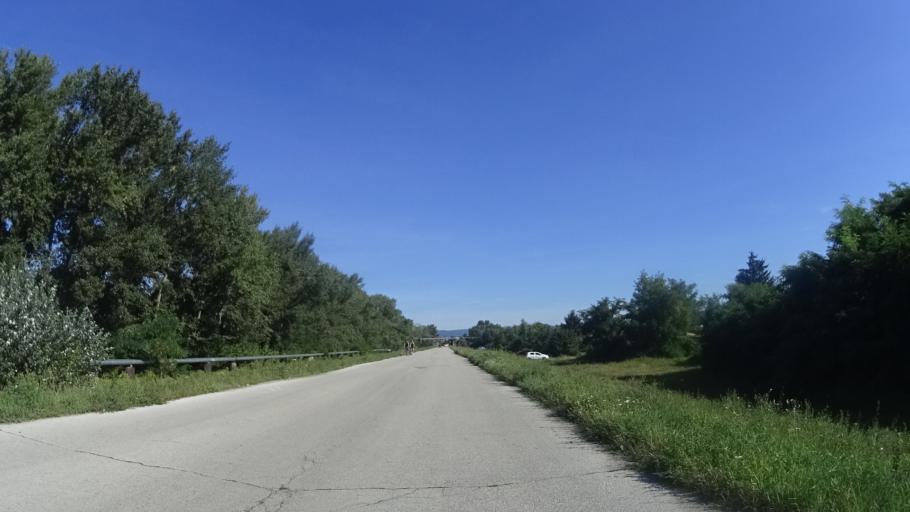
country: SK
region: Bratislavsky
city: Bratislava
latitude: 48.1254
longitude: 17.1596
